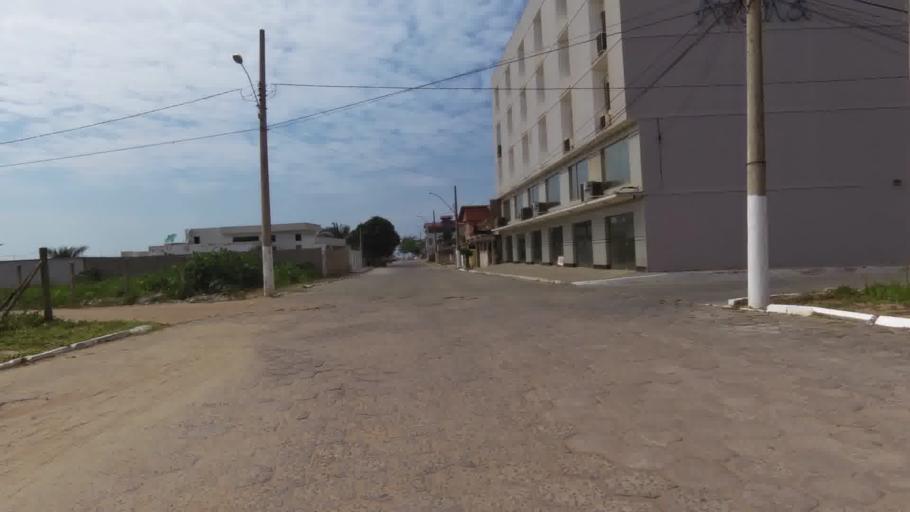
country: BR
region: Espirito Santo
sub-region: Marataizes
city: Marataizes
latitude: -21.0247
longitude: -40.8151
